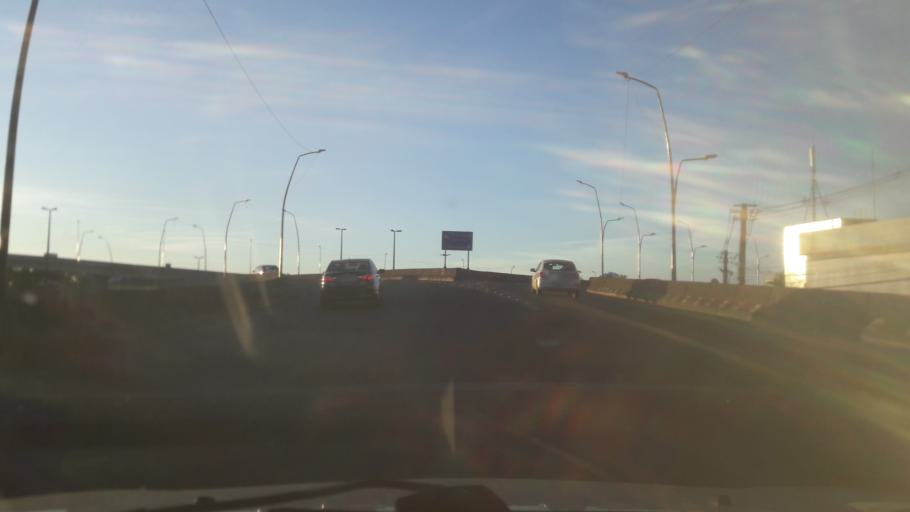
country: BR
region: Rio Grande do Sul
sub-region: Porto Alegre
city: Porto Alegre
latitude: -29.9875
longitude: -51.1806
